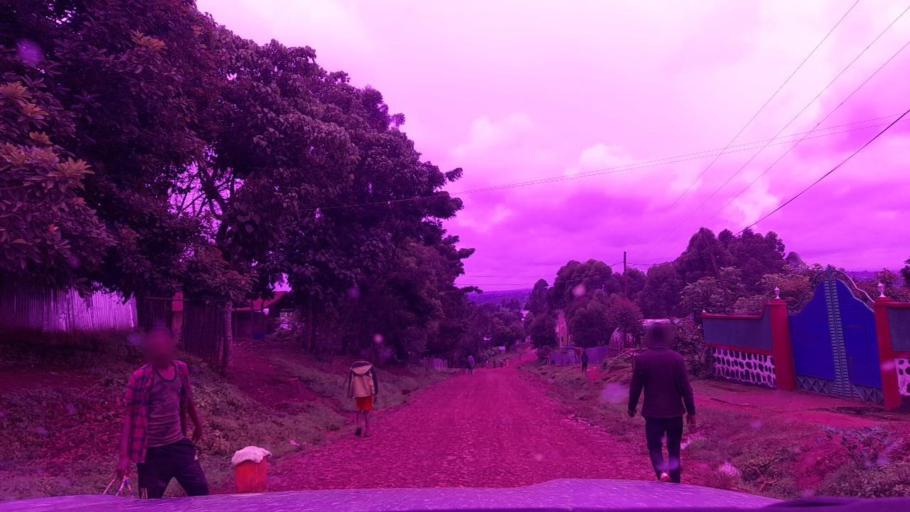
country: ET
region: Southern Nations, Nationalities, and People's Region
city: Tippi
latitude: 7.5921
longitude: 35.7489
